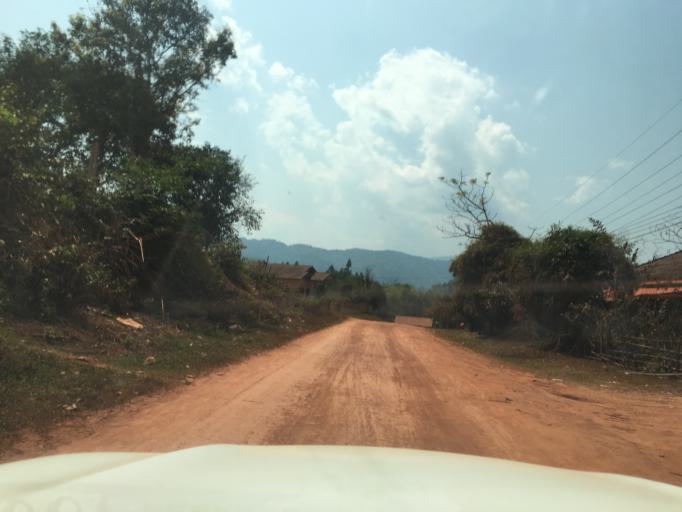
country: LA
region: Bolikhamxai
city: Bolikhan
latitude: 18.7490
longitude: 103.5933
